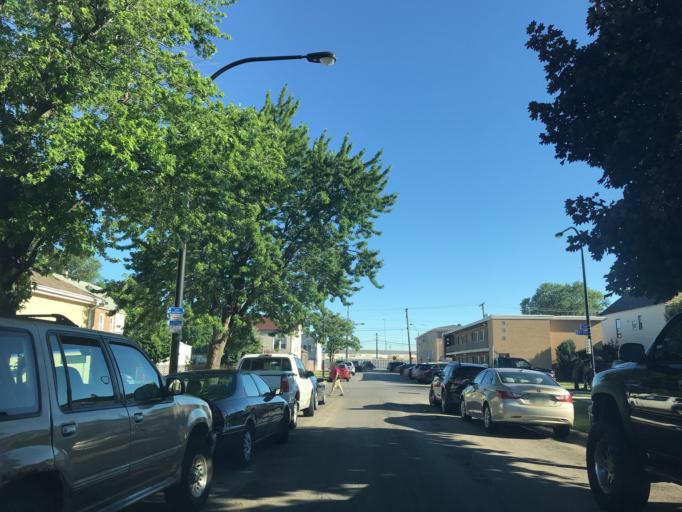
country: US
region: Illinois
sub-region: Cook County
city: Cicero
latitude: 41.8450
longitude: -87.7613
